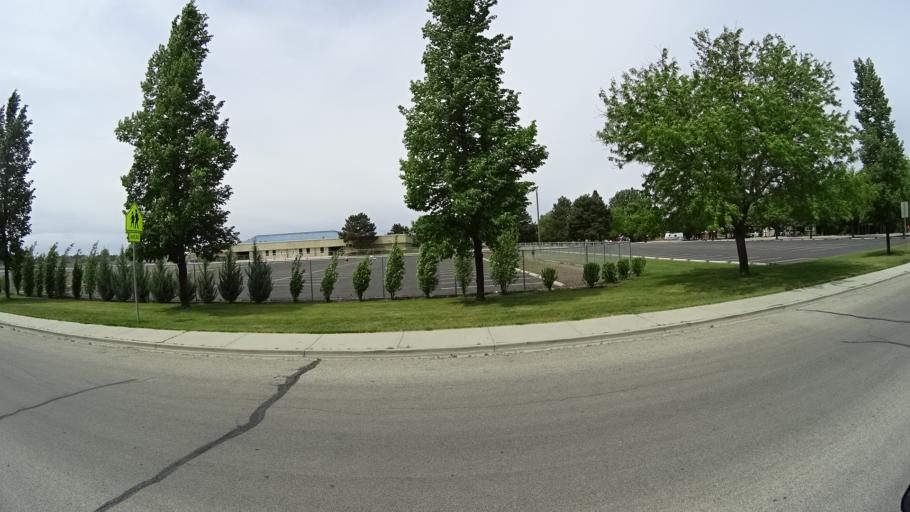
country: US
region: Idaho
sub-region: Ada County
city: Meridian
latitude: 43.5532
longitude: -116.3243
